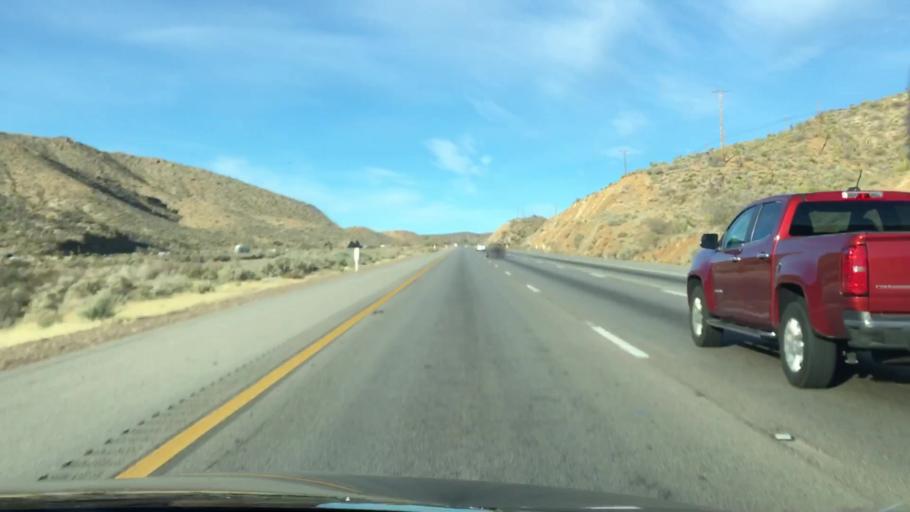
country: US
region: Nevada
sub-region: Clark County
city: Sandy Valley
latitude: 35.4691
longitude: -115.4923
